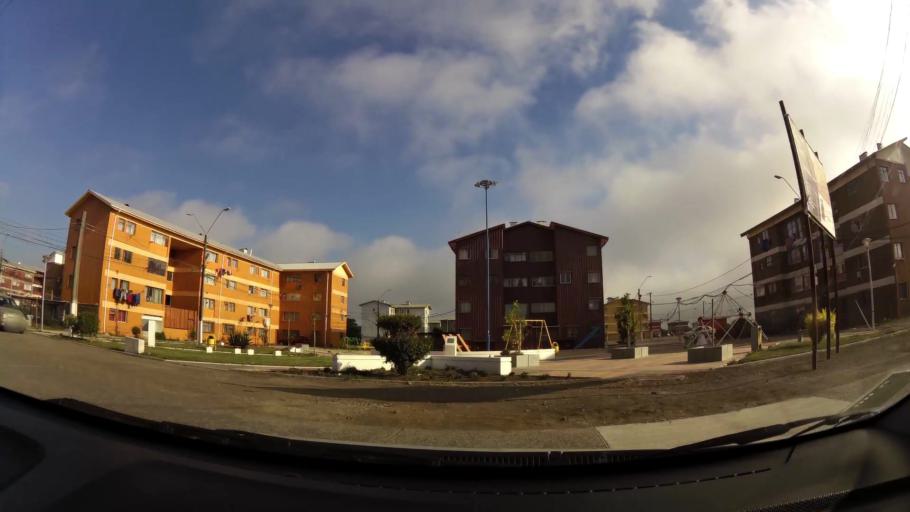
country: CL
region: Biobio
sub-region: Provincia de Concepcion
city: Concepcion
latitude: -36.7902
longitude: -73.0937
